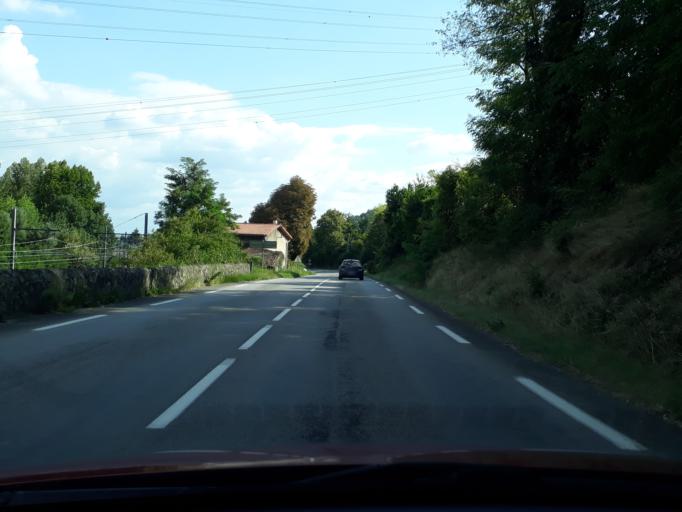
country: FR
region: Rhone-Alpes
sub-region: Departement de la Loire
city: Saint-Pierre-de-Boeuf
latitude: 45.3680
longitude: 4.7523
